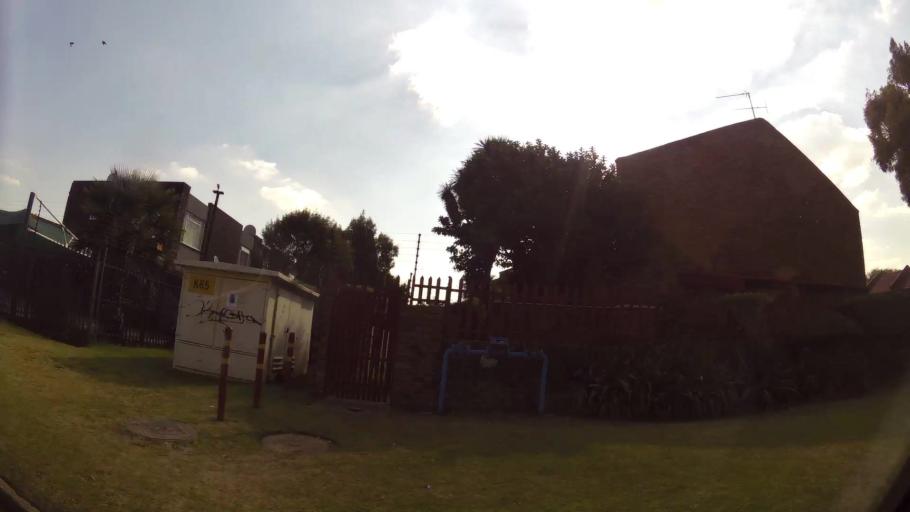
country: ZA
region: Gauteng
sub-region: Ekurhuleni Metropolitan Municipality
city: Boksburg
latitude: -26.1911
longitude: 28.2322
